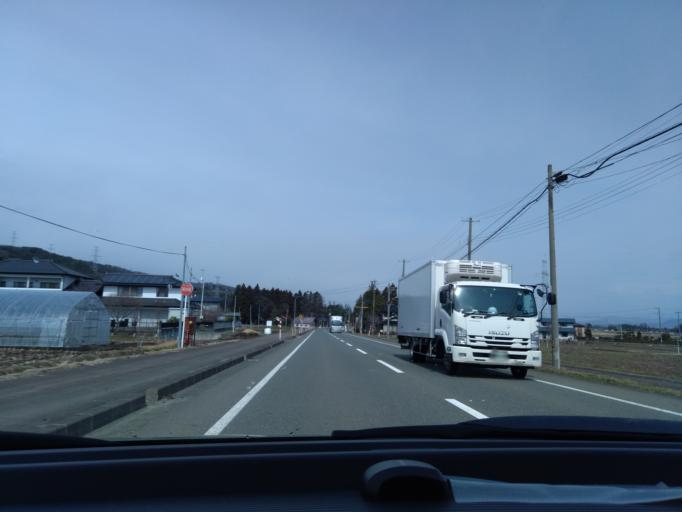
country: JP
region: Iwate
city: Morioka-shi
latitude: 39.5856
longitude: 141.1087
